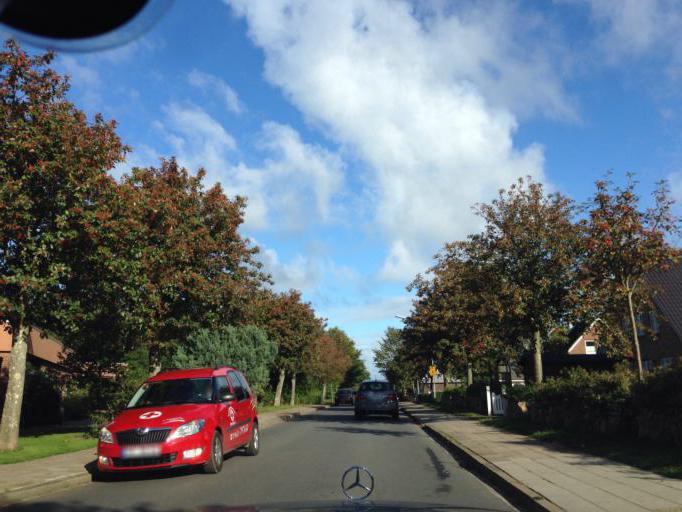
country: DE
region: Schleswig-Holstein
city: Wyk auf Fohr
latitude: 54.6904
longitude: 8.5594
